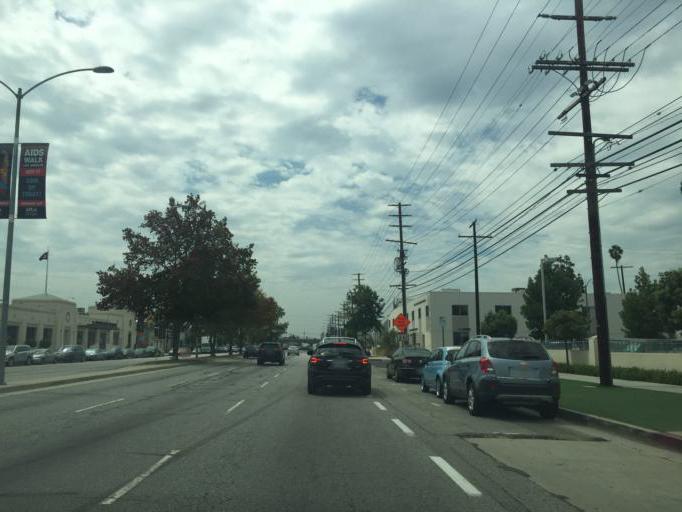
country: US
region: California
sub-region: Los Angeles County
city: Culver City
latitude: 34.0311
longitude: -118.3854
